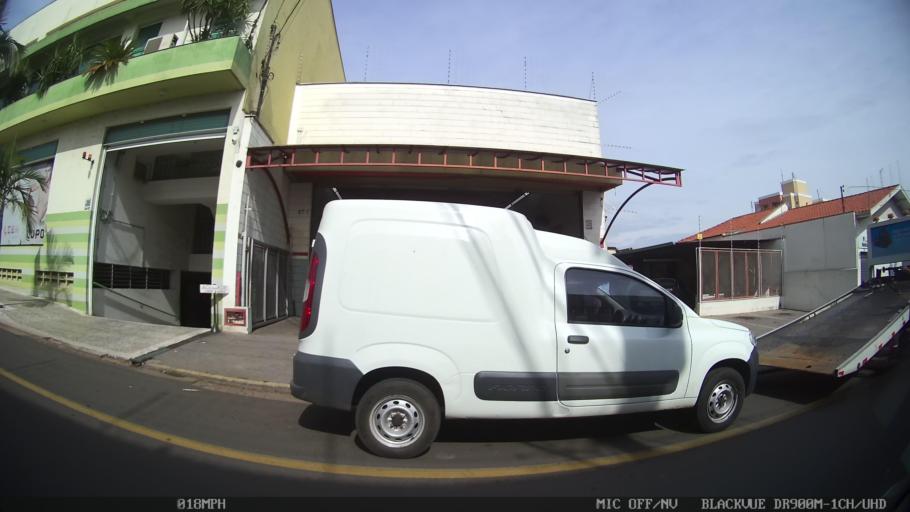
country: BR
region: Sao Paulo
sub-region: Piracicaba
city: Piracicaba
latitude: -22.7385
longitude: -47.6605
